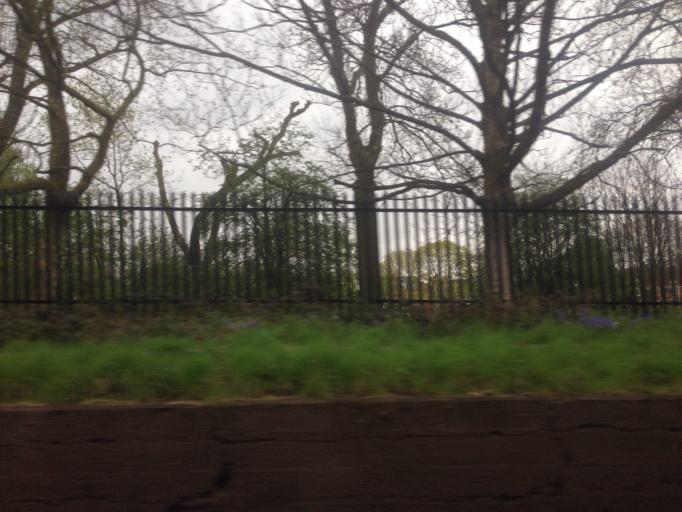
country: GB
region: England
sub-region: Greater London
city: Earlsfield
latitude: 51.4487
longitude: -0.1663
